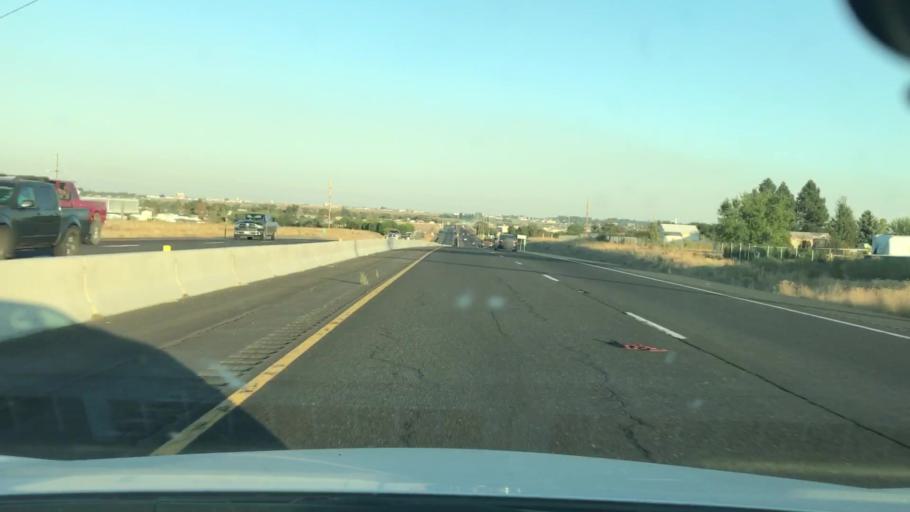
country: US
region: Washington
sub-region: Grant County
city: Cascade Valley
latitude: 47.1528
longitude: -119.3034
